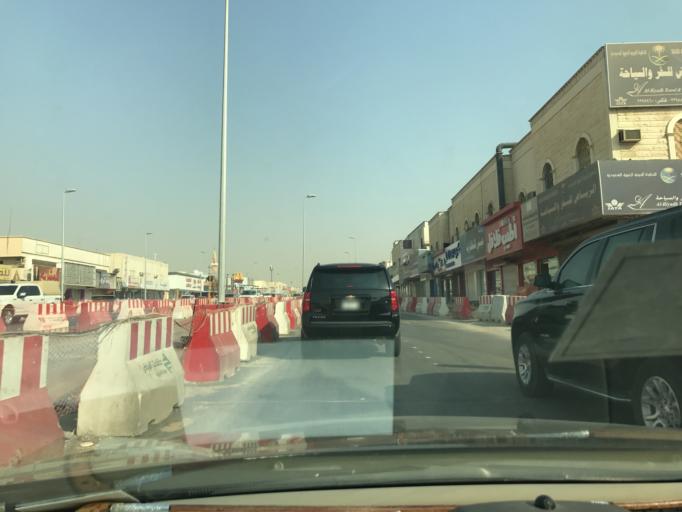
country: SA
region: Ar Riyad
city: Riyadh
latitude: 24.7519
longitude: 46.7711
